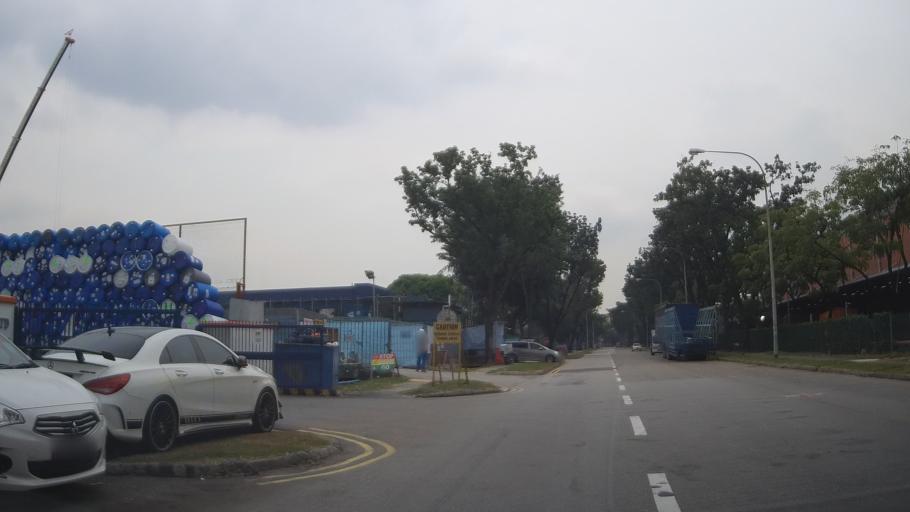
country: MY
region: Johor
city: Johor Bahru
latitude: 1.3130
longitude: 103.6599
